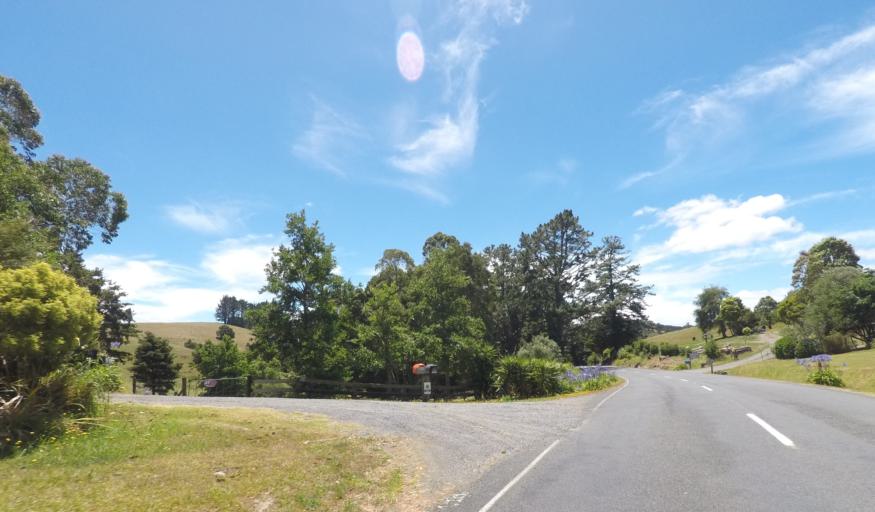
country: NZ
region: Northland
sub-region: Whangarei
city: Whangarei
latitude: -35.5448
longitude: 174.3065
